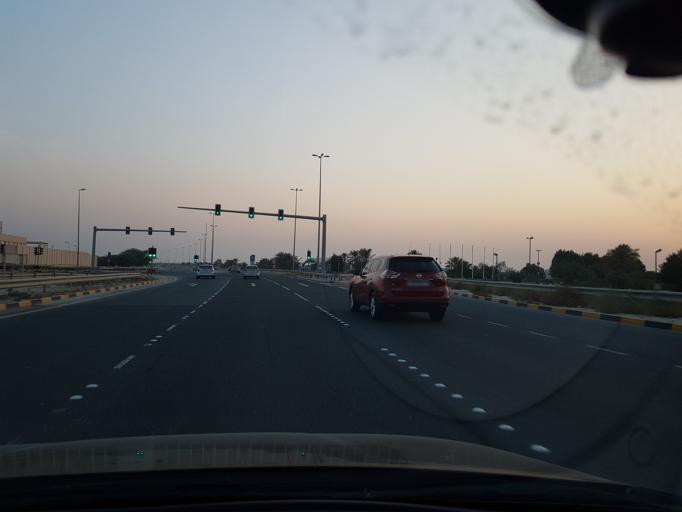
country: BH
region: Central Governorate
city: Dar Kulayb
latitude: 26.0254
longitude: 50.4936
